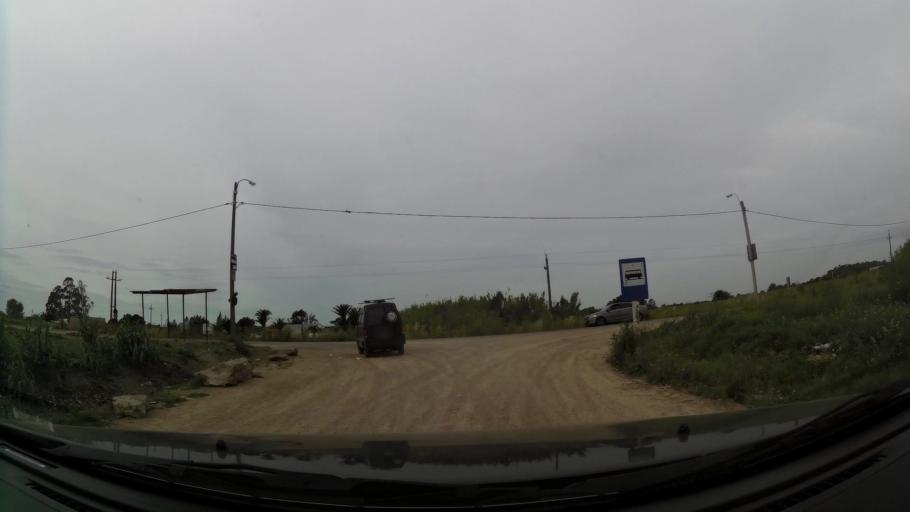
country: UY
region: Canelones
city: La Paz
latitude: -34.7498
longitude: -56.2145
